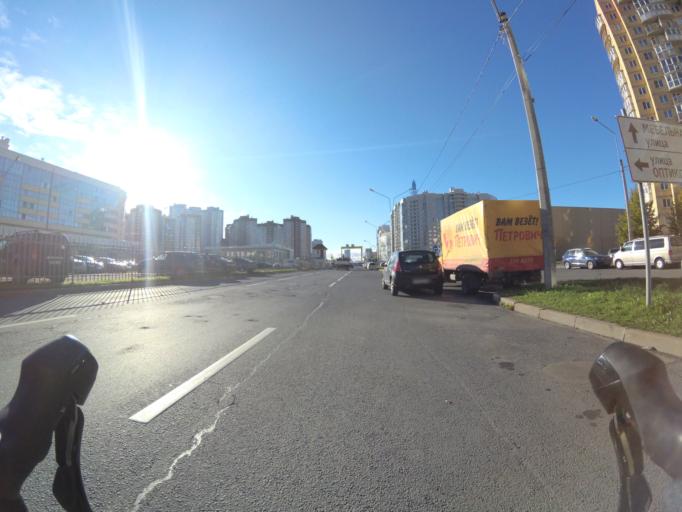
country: RU
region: Leningrad
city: Untolovo
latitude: 60.0027
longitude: 30.2101
